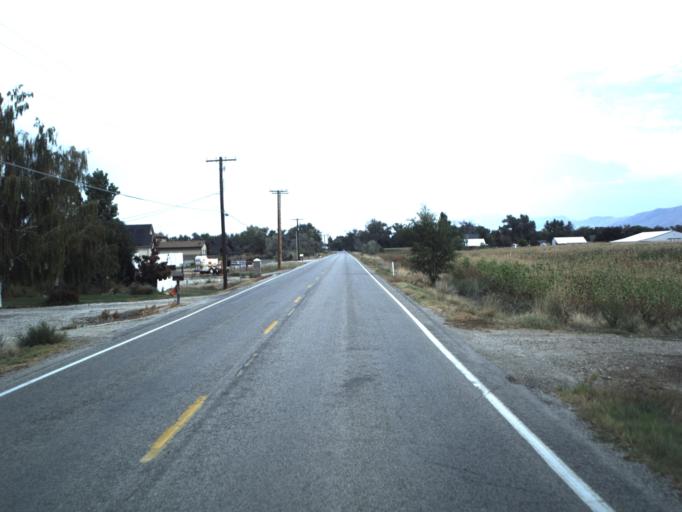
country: US
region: Utah
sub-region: Weber County
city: Plain City
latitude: 41.2705
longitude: -112.0923
